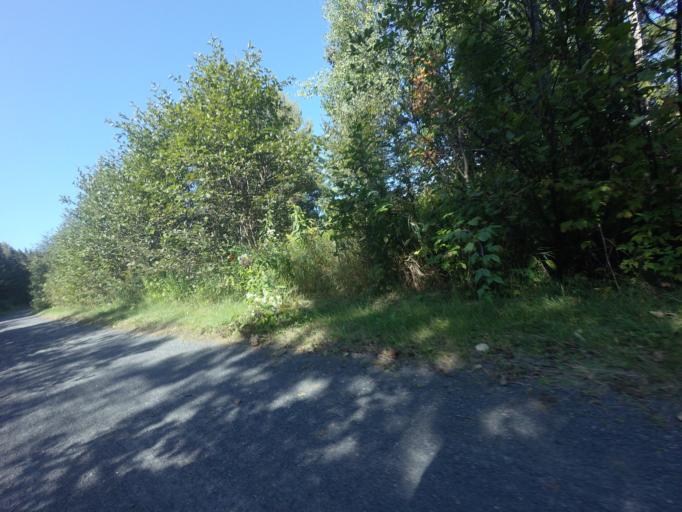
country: CA
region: Quebec
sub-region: Laurentides
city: Sainte-Agathe-des-Monts
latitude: 46.0837
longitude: -74.3358
